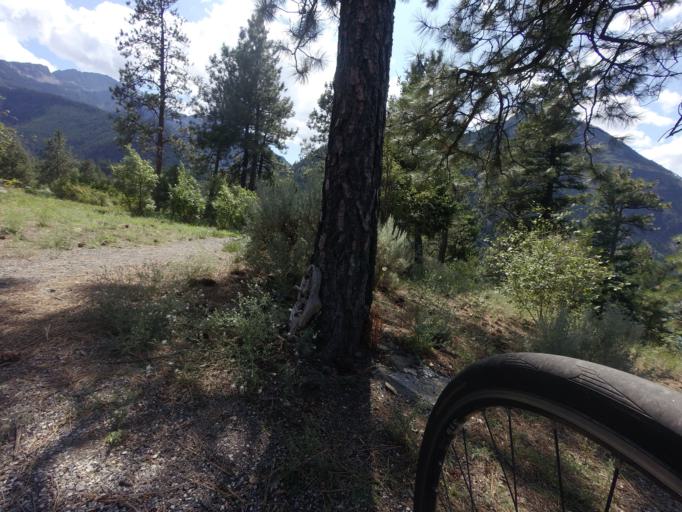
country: CA
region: British Columbia
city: Lillooet
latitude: 50.6680
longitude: -121.9870
